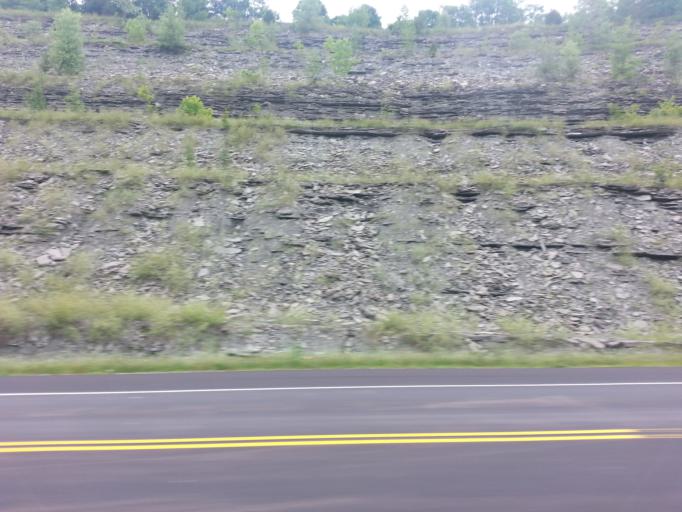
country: US
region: Ohio
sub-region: Brown County
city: Aberdeen
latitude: 38.6798
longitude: -83.7944
